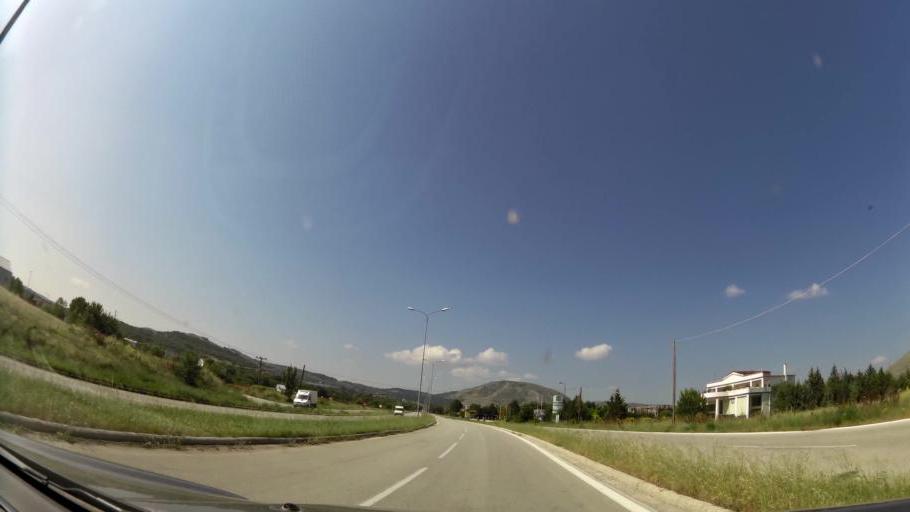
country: GR
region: West Macedonia
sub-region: Nomos Kozanis
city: Koila
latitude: 40.3404
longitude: 21.7939
